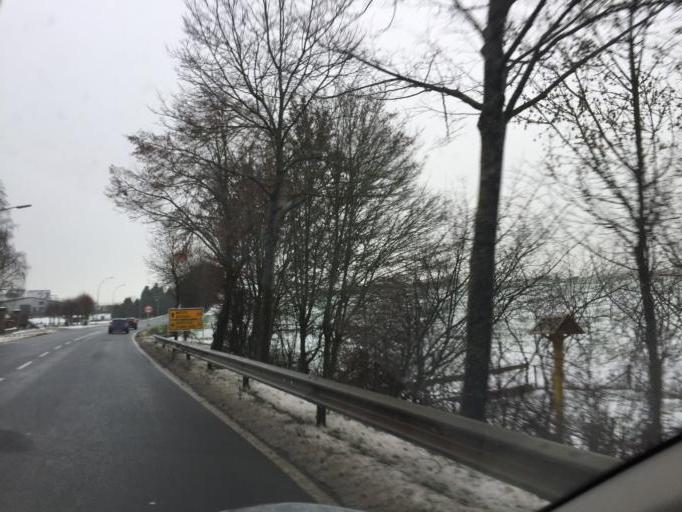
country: LU
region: Diekirch
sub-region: Canton de Diekirch
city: Niederfeulen
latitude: 49.8520
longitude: 6.0394
